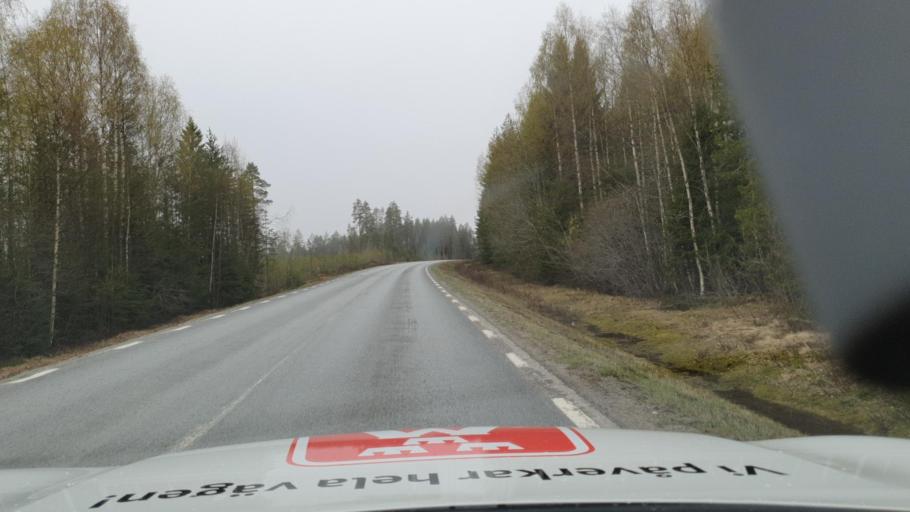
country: SE
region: Vaesterbotten
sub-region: Vannas Kommun
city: Vaennaes
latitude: 63.7751
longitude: 19.7250
